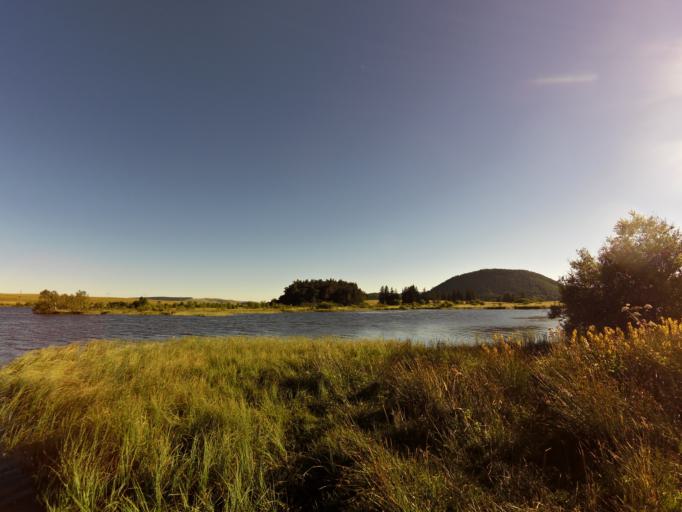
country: FR
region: Auvergne
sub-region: Departement du Puy-de-Dome
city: Mont-Dore
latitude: 45.4702
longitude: 2.9233
